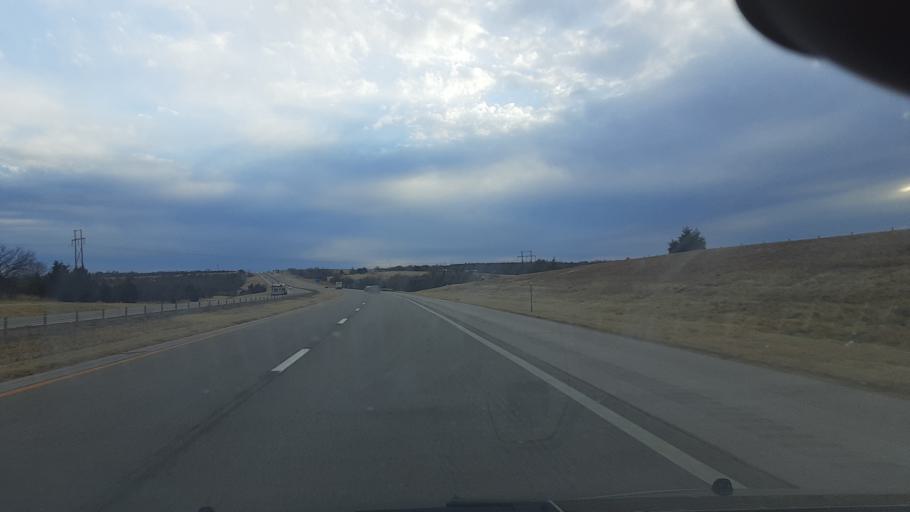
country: US
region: Oklahoma
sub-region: Logan County
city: Guthrie
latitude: 35.9082
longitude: -97.3934
